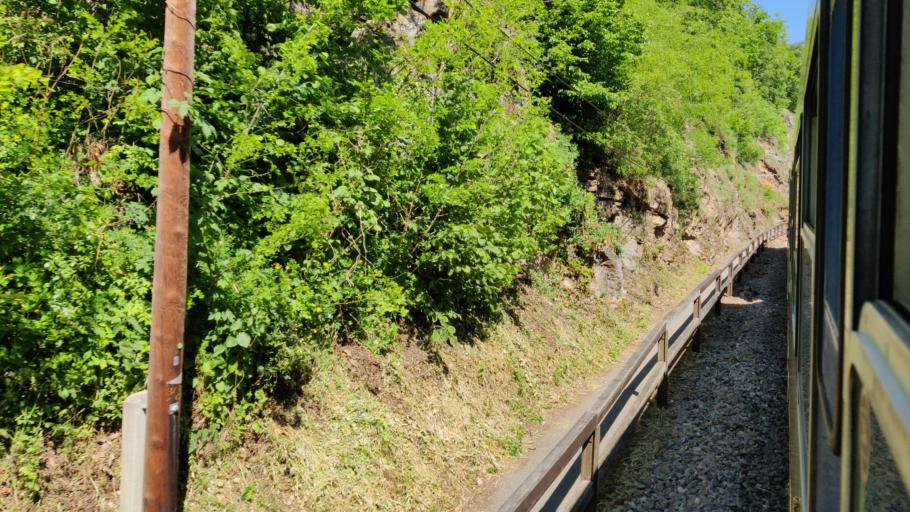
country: AT
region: Lower Austria
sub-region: Politischer Bezirk Horn
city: Gars am Kamp
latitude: 48.6024
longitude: 15.6536
